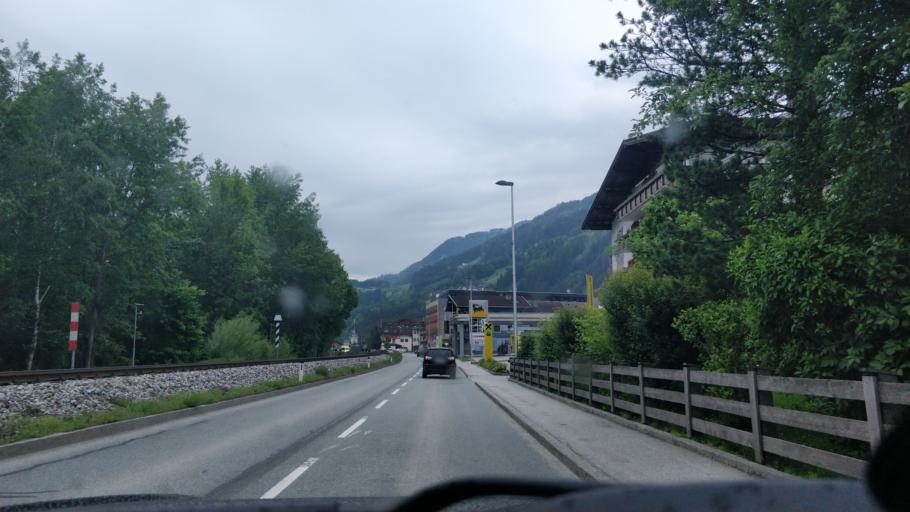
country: AT
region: Tyrol
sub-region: Politischer Bezirk Schwaz
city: Ried im Zillertal
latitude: 47.2957
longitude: 11.8749
